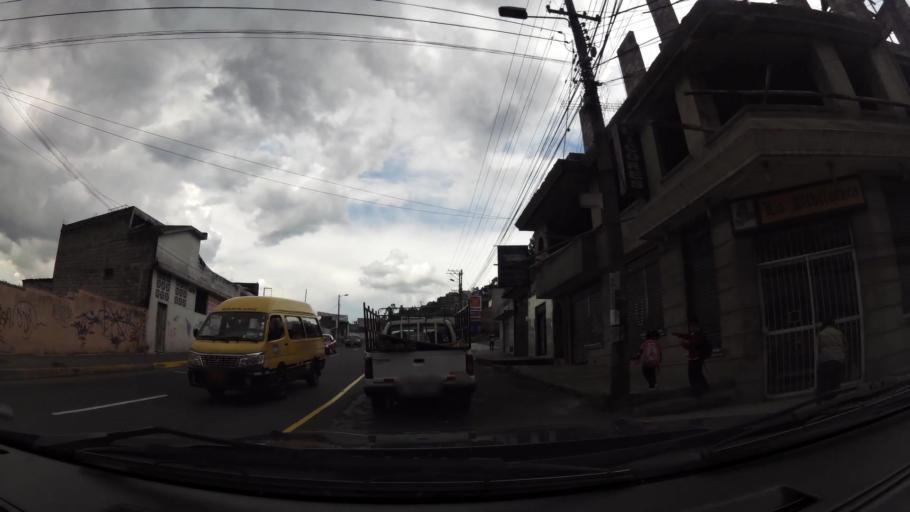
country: EC
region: Pichincha
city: Quito
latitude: -0.2473
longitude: -78.5064
